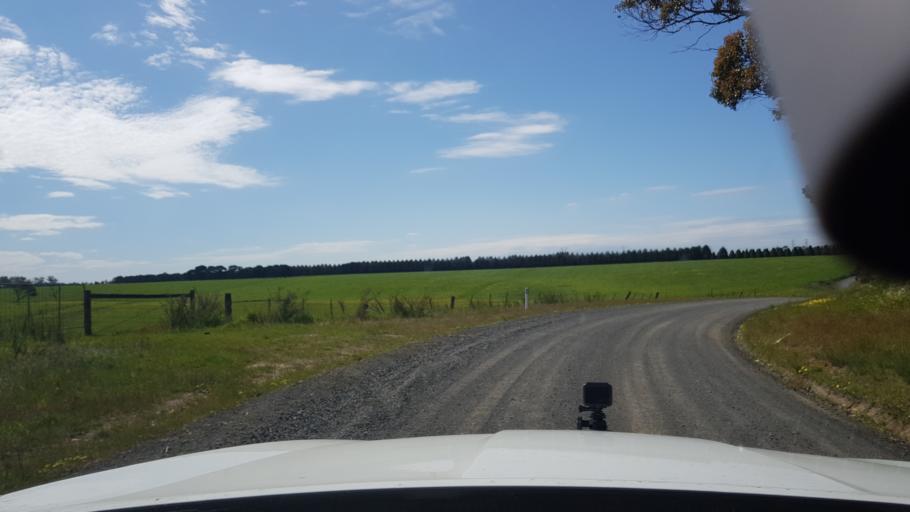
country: AU
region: Victoria
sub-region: Latrobe
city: Moe
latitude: -38.1328
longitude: 146.1082
